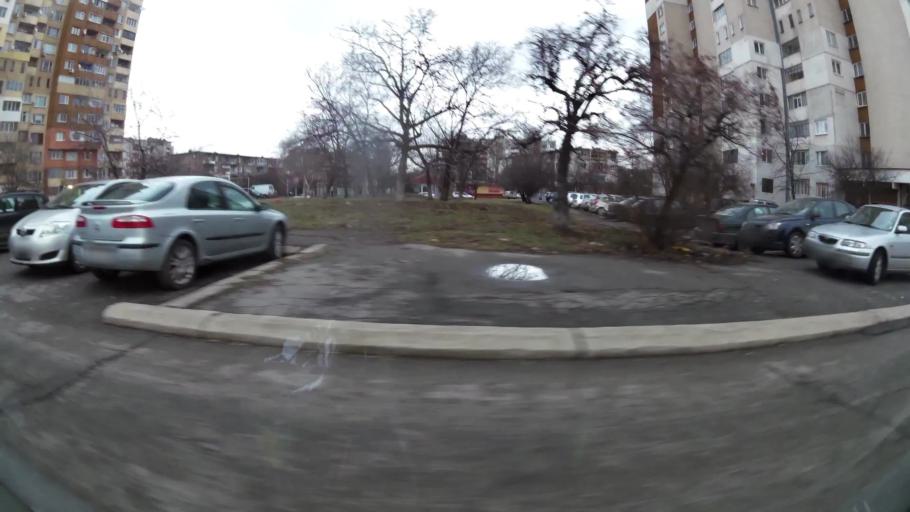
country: BG
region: Sofia-Capital
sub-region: Stolichna Obshtina
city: Sofia
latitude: 42.7349
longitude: 23.2971
